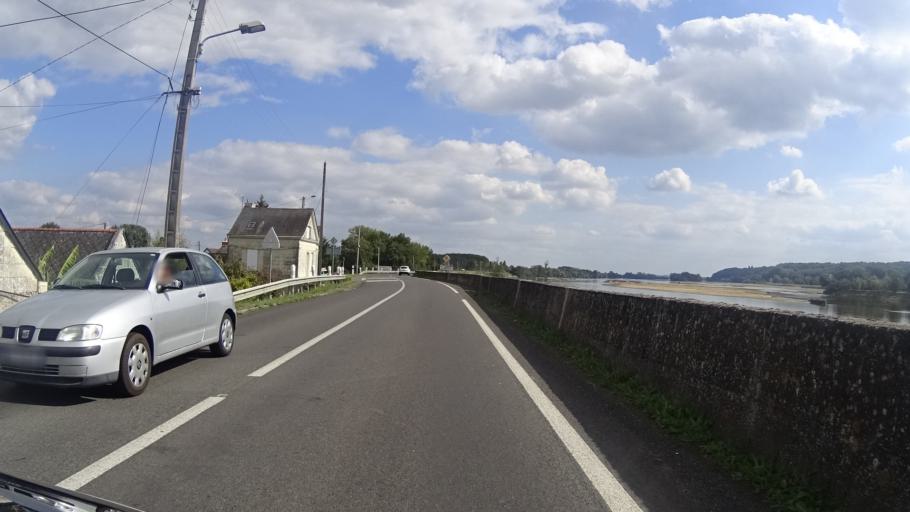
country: FR
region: Pays de la Loire
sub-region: Departement de Maine-et-Loire
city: Saint-Clement-des-Levees
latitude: 47.3257
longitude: -0.1743
